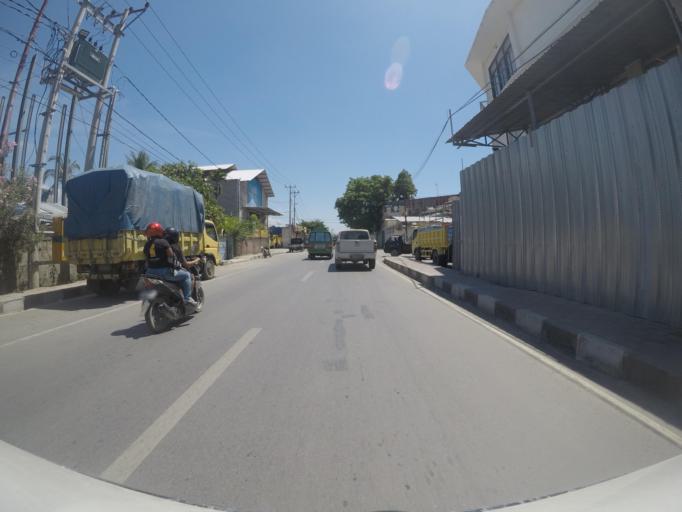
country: TL
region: Dili
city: Dili
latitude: -8.5552
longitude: 125.5878
